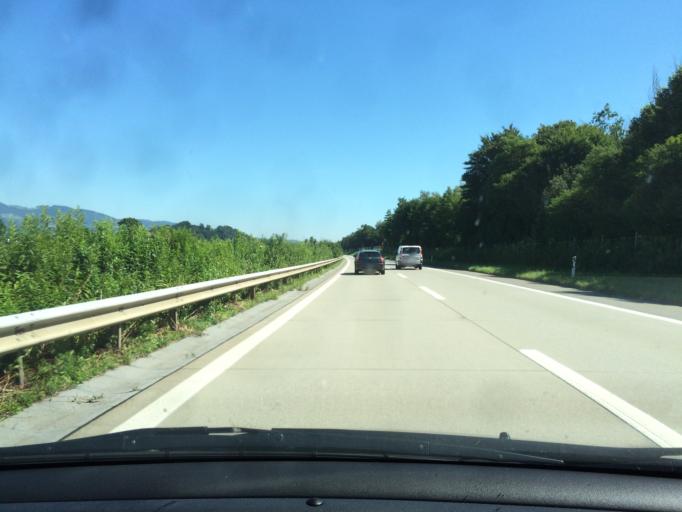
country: CH
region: Saint Gallen
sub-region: Wahlkreis Rheintal
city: Oberriet
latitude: 47.3192
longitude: 9.5858
